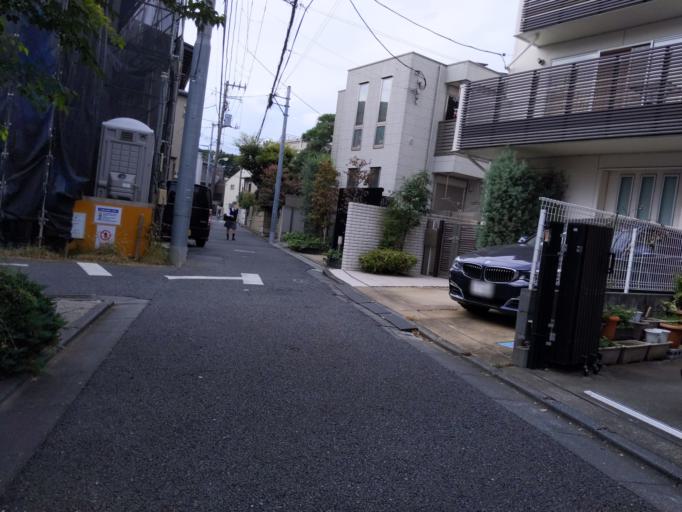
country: JP
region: Tokyo
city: Tokyo
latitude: 35.6585
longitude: 139.6645
